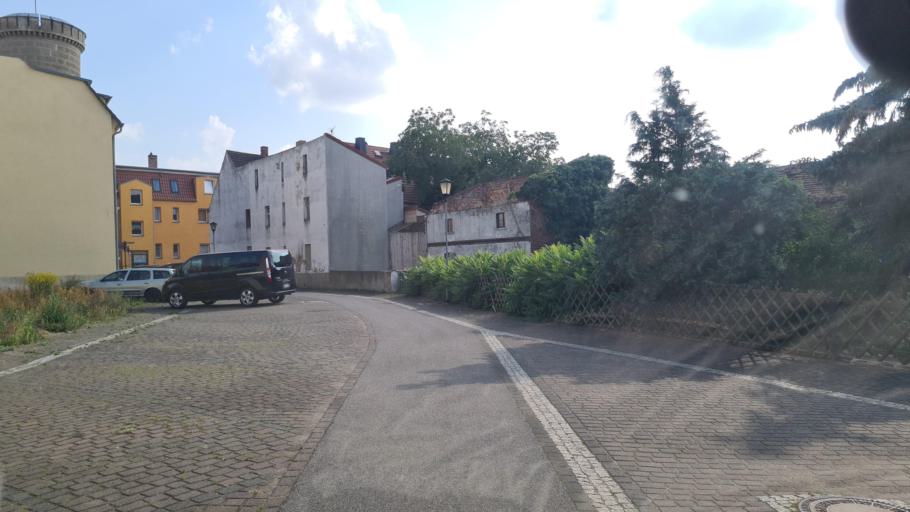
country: DE
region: Brandenburg
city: Dahme
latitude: 51.8695
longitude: 13.4228
